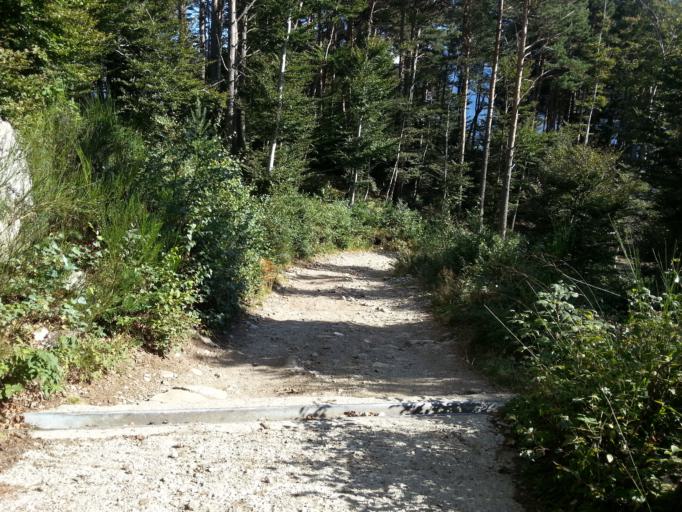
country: IT
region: Lombardy
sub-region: Provincia di Como
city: Montemezzo
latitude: 46.1986
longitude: 9.3816
